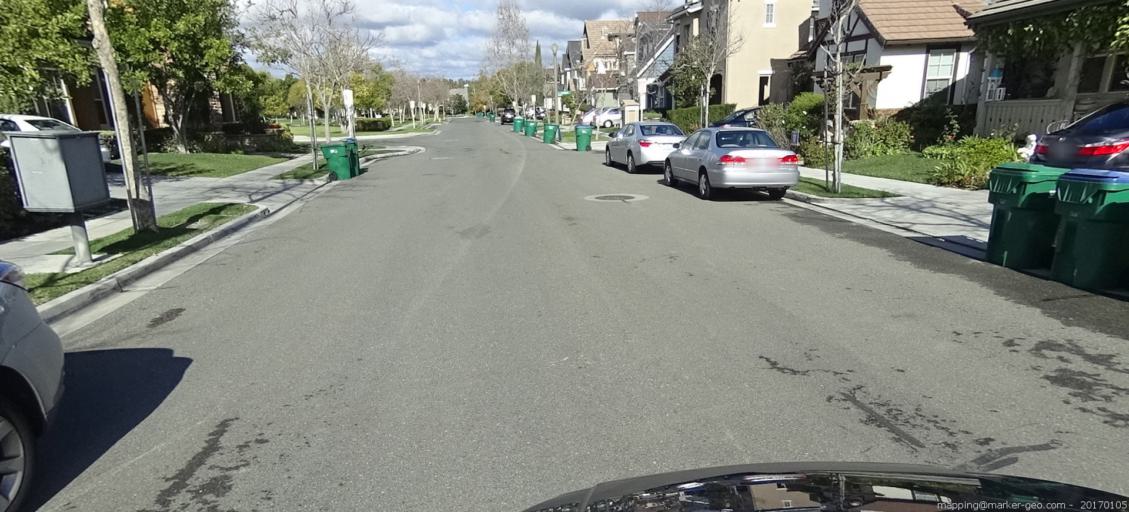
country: US
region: California
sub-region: Orange County
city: Ladera Ranch
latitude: 33.5444
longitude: -117.6353
